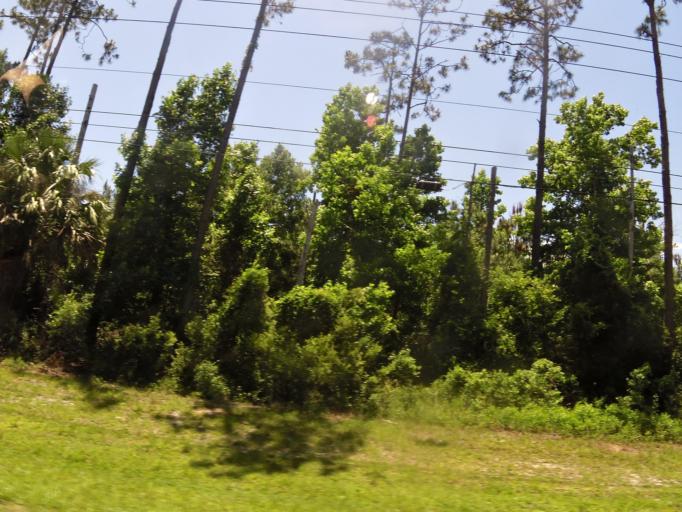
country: US
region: Florida
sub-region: Flagler County
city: Flagler Beach
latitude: 29.4666
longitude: -81.1734
